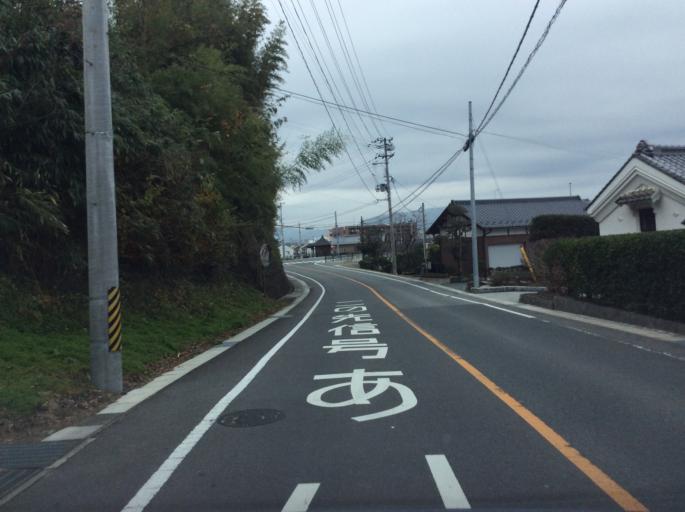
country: JP
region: Fukushima
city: Iwaki
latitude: 37.0493
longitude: 140.9147
